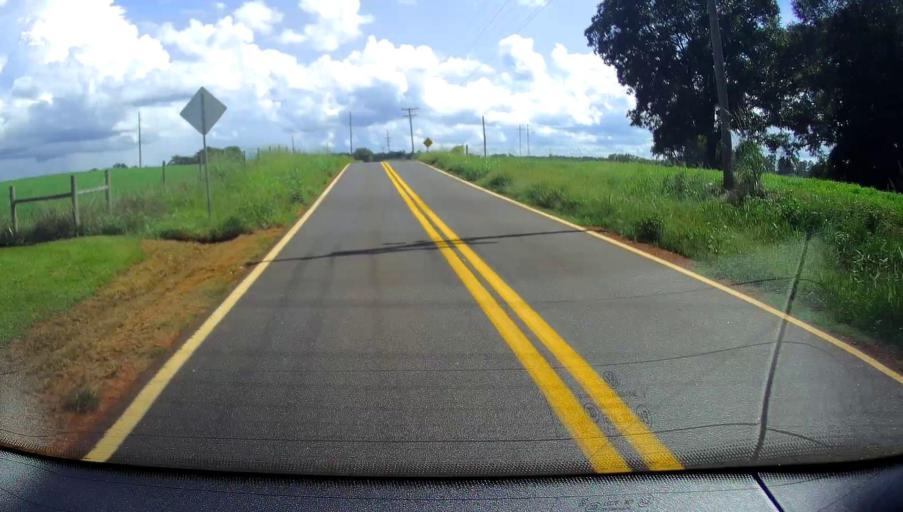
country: US
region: Georgia
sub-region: Upson County
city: Hannahs Mill
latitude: 32.9483
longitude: -84.2902
